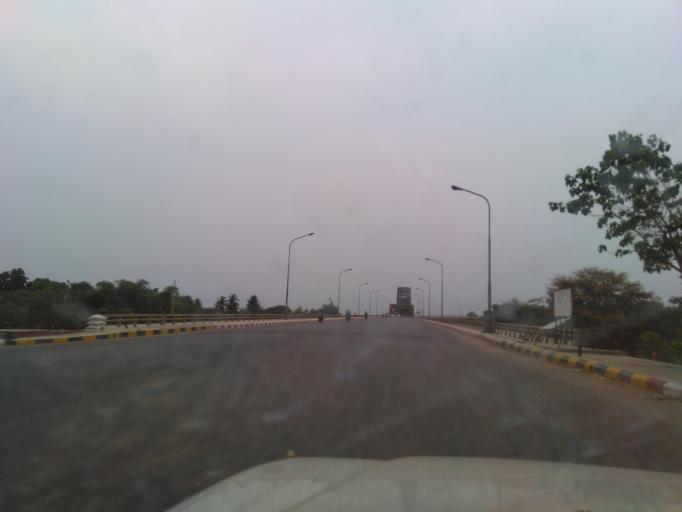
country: MM
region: Sagain
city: Sagaing
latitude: 21.8729
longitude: 96.0044
